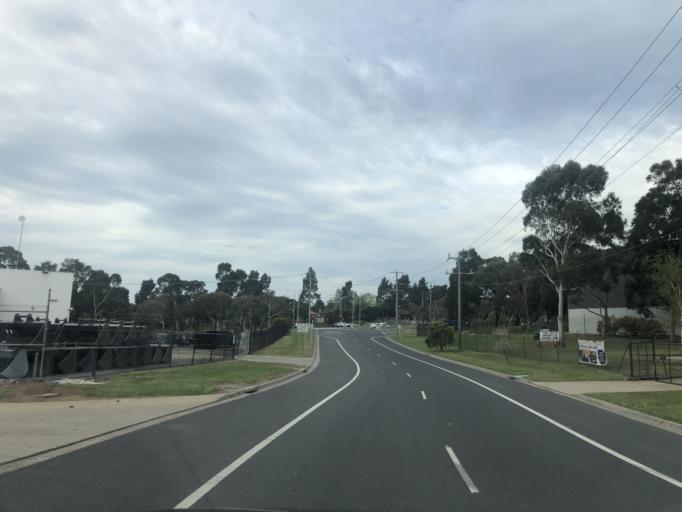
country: AU
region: Victoria
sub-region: Casey
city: Hallam
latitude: -38.0064
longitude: 145.2627
